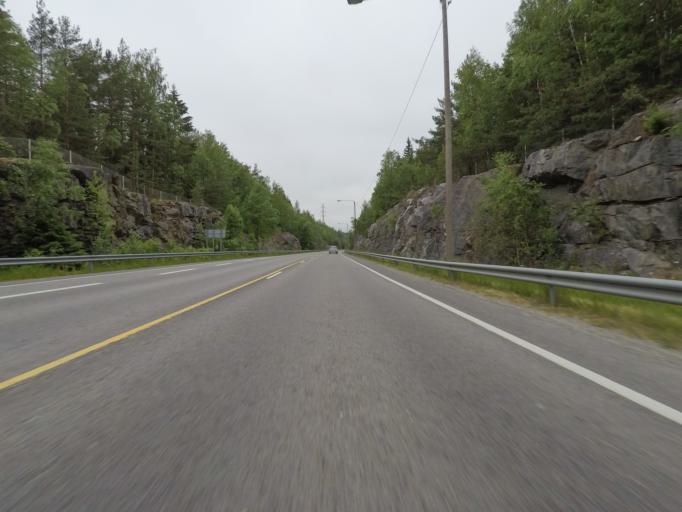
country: FI
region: Varsinais-Suomi
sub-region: Turku
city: Raisio
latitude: 60.4623
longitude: 22.1464
